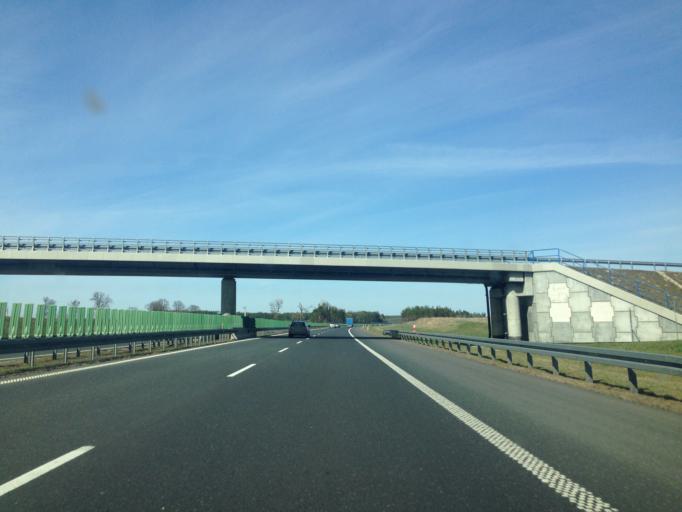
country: PL
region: Pomeranian Voivodeship
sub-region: Powiat starogardzki
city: Smetowo Graniczne
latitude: 53.7965
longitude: 18.6254
